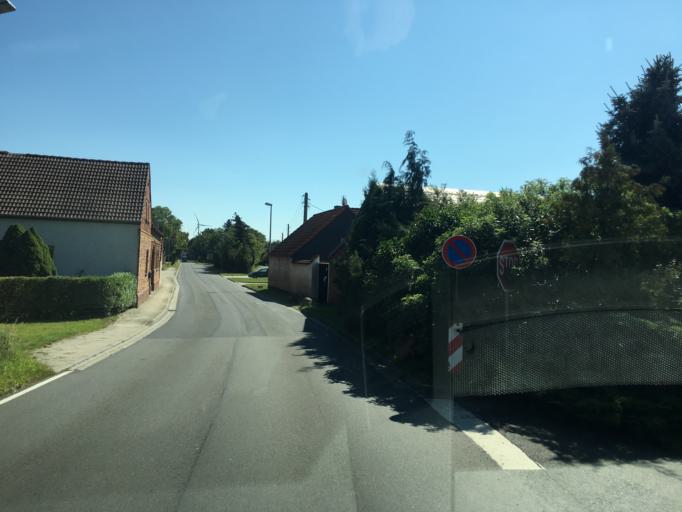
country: DE
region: Brandenburg
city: Welzow
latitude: 51.5582
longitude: 14.1297
